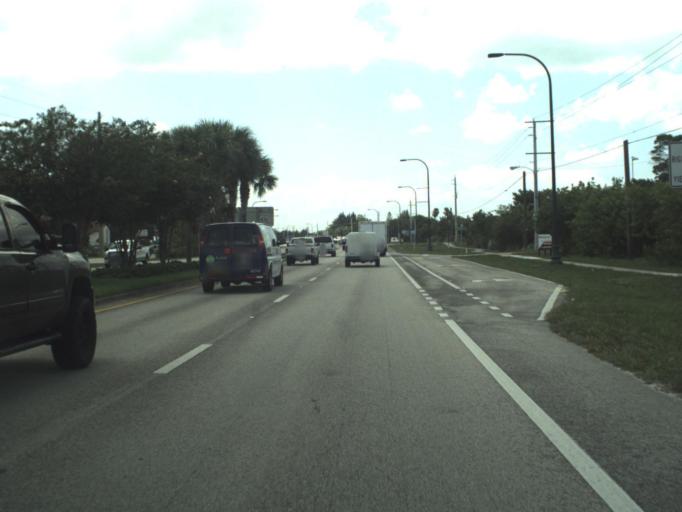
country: US
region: Florida
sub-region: Martin County
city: Hobe Sound
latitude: 27.0793
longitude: -80.1451
